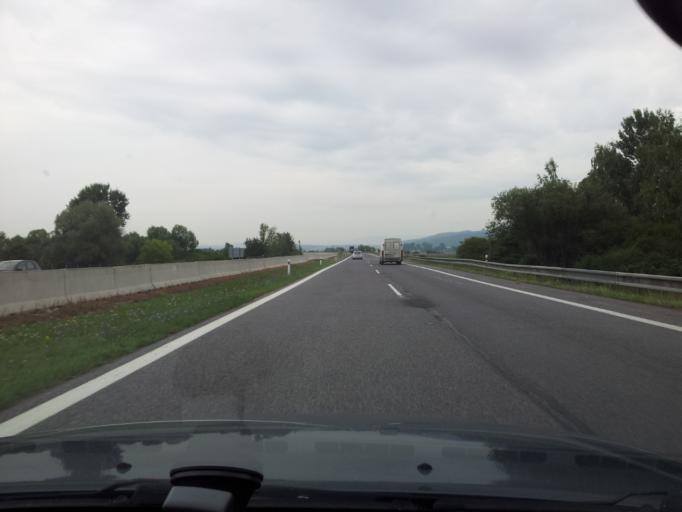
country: SK
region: Banskobystricky
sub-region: Okres Banska Bystrica
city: Zvolen
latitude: 48.6023
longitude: 19.1160
